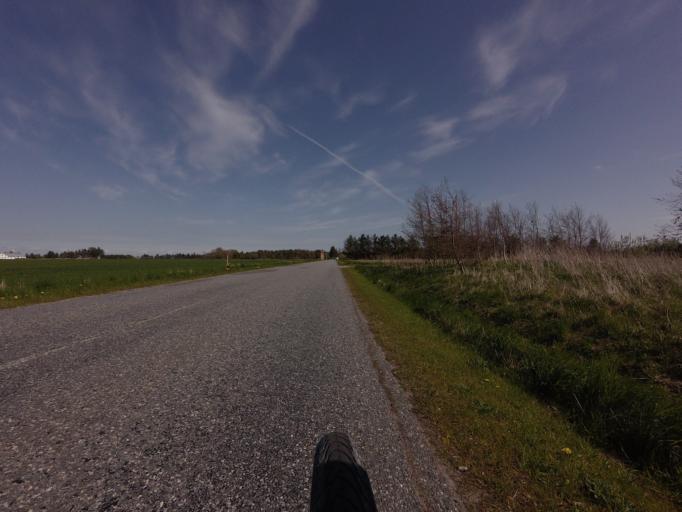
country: DK
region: North Denmark
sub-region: Jammerbugt Kommune
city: Pandrup
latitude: 57.2259
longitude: 9.6417
